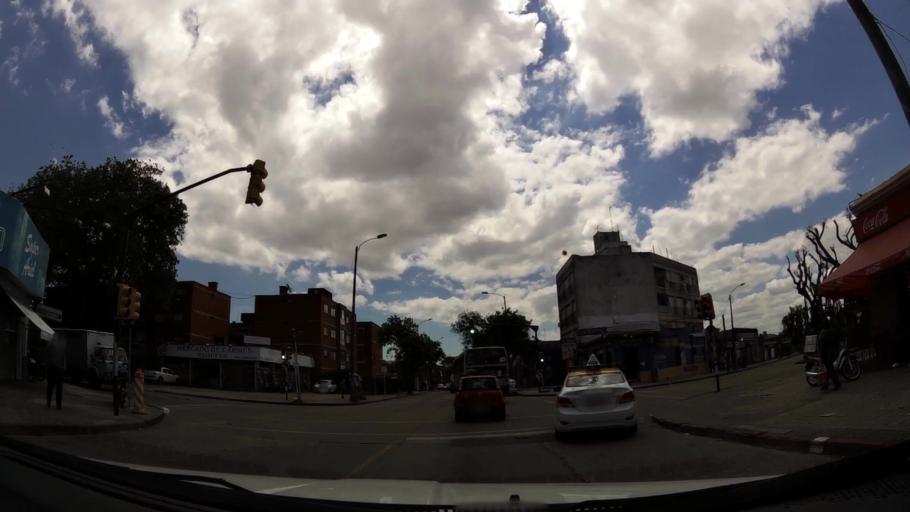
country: UY
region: Montevideo
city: Montevideo
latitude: -34.8422
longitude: -56.2086
